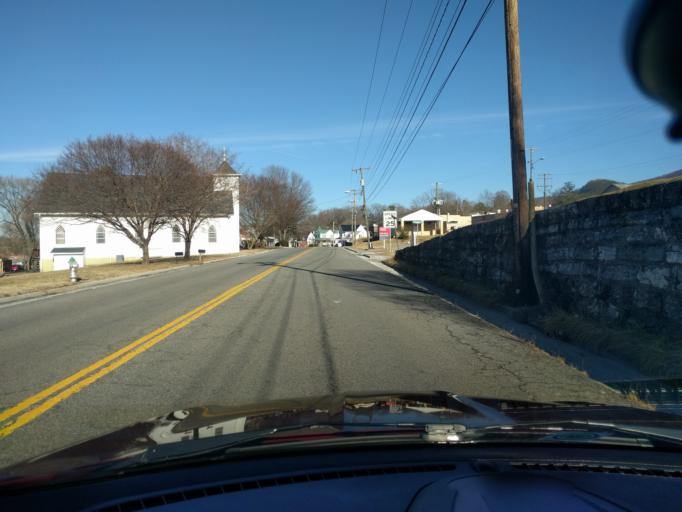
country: US
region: Virginia
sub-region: Botetourt County
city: Buchanan
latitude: 37.5231
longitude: -79.6857
